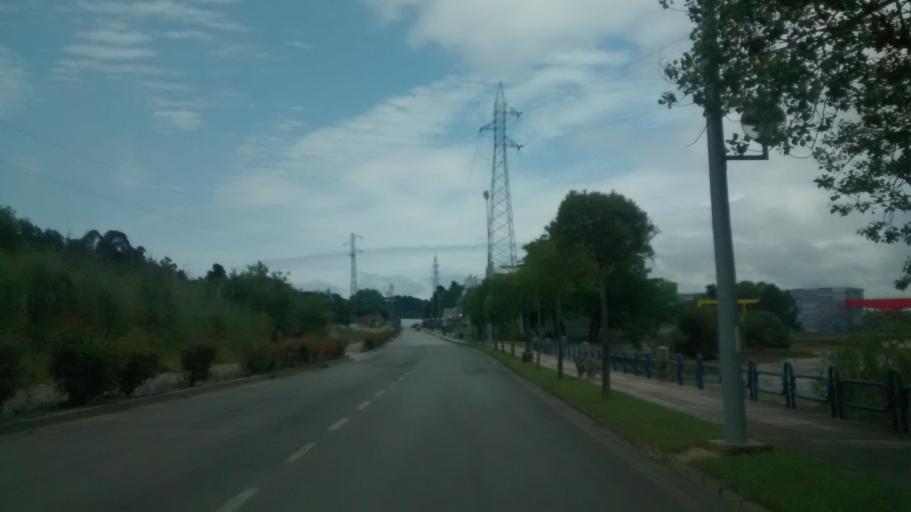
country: ES
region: Cantabria
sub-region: Provincia de Cantabria
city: El Astillero
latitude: 43.4131
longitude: -3.8269
